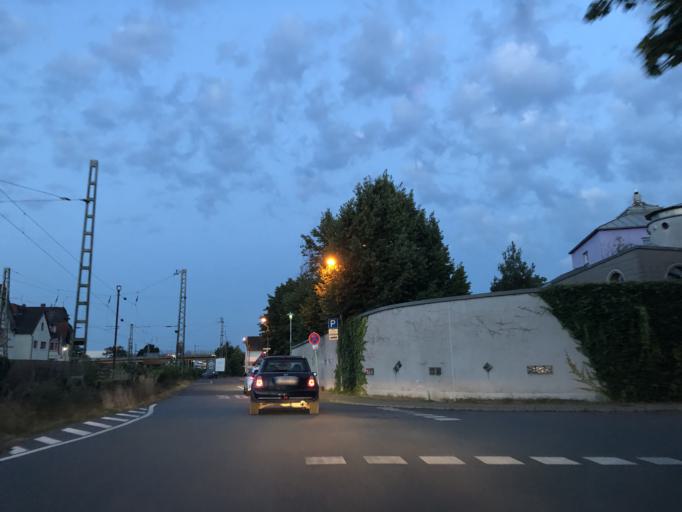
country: DE
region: Hesse
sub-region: Regierungsbezirk Darmstadt
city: Gross-Gerau
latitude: 49.9255
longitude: 8.4813
